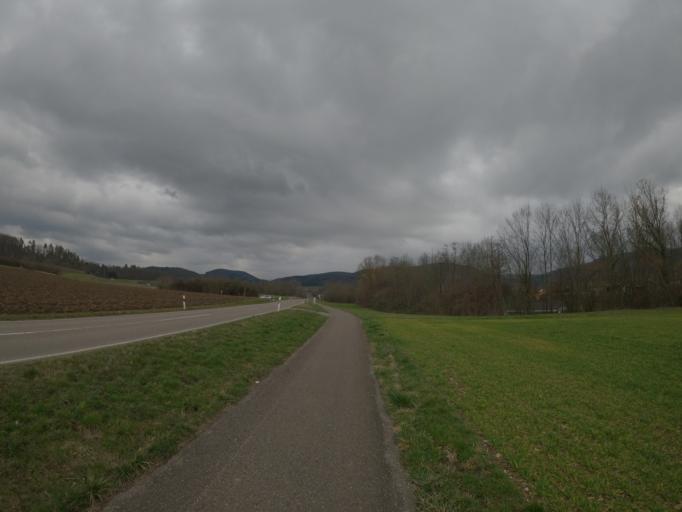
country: DE
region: Baden-Wuerttemberg
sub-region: Regierungsbezirk Stuttgart
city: Schlat
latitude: 48.6631
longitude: 9.7011
